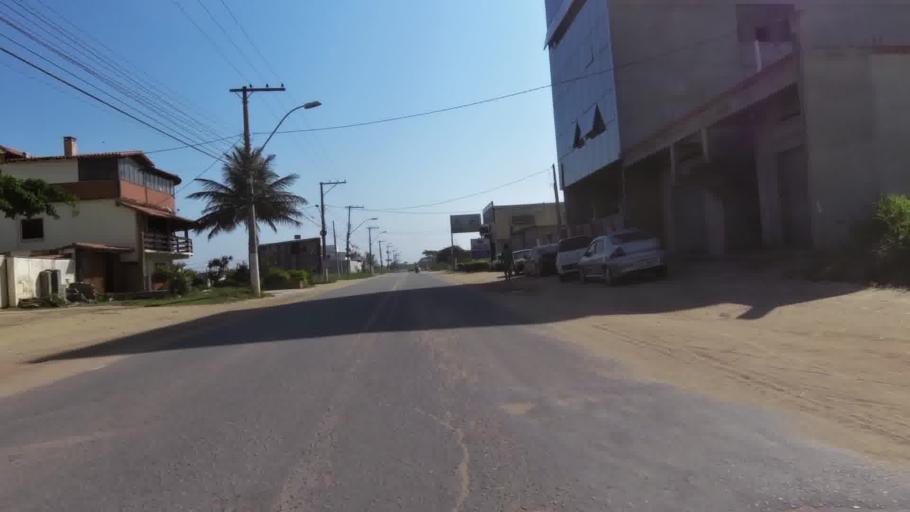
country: BR
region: Espirito Santo
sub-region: Marataizes
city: Marataizes
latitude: -21.0459
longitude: -40.8399
